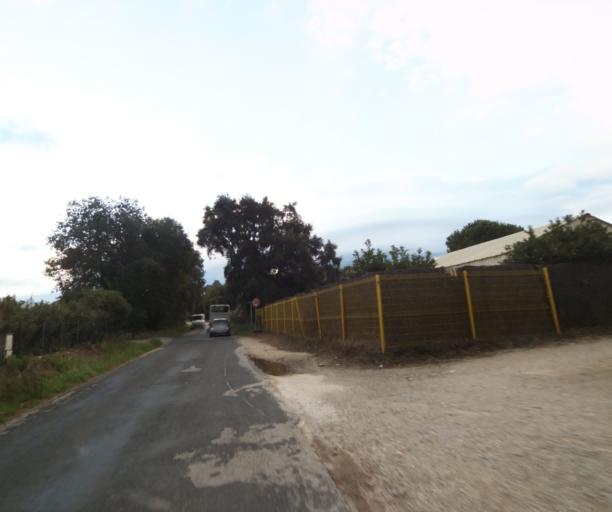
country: FR
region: Languedoc-Roussillon
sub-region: Departement des Pyrenees-Orientales
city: Argelers
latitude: 42.5591
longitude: 3.0216
